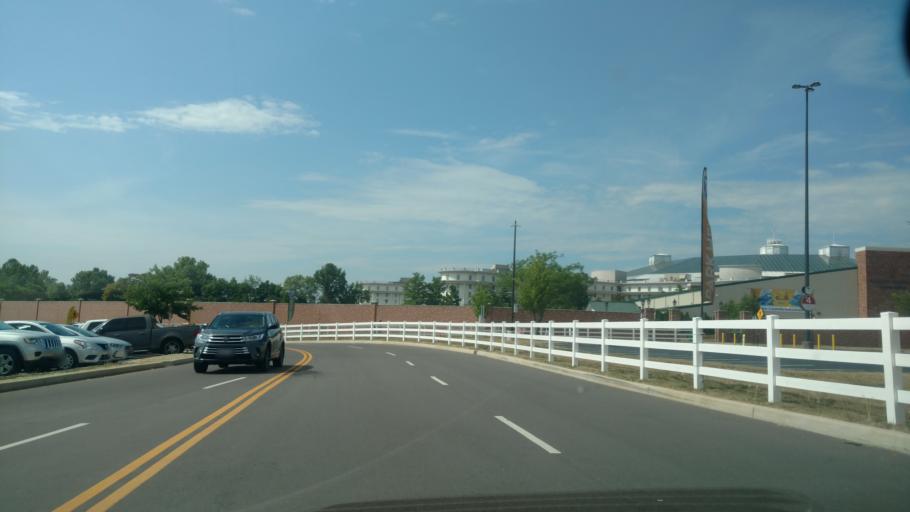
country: US
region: Tennessee
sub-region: Davidson County
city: Lakewood
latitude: 36.2083
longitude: -86.6957
